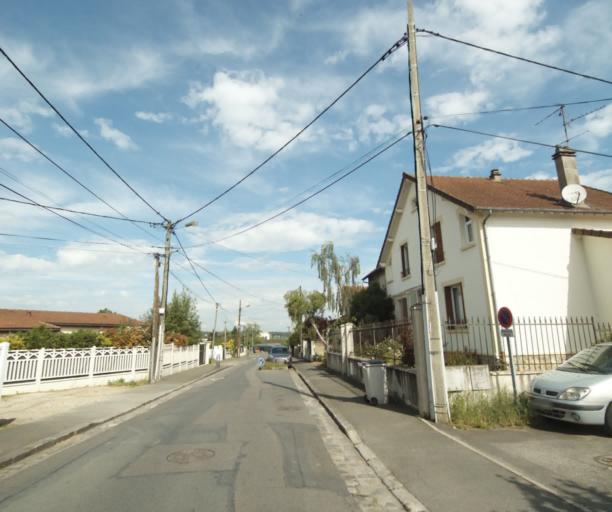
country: FR
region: Ile-de-France
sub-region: Departement des Yvelines
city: Les Mureaux
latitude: 48.9924
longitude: 1.9210
